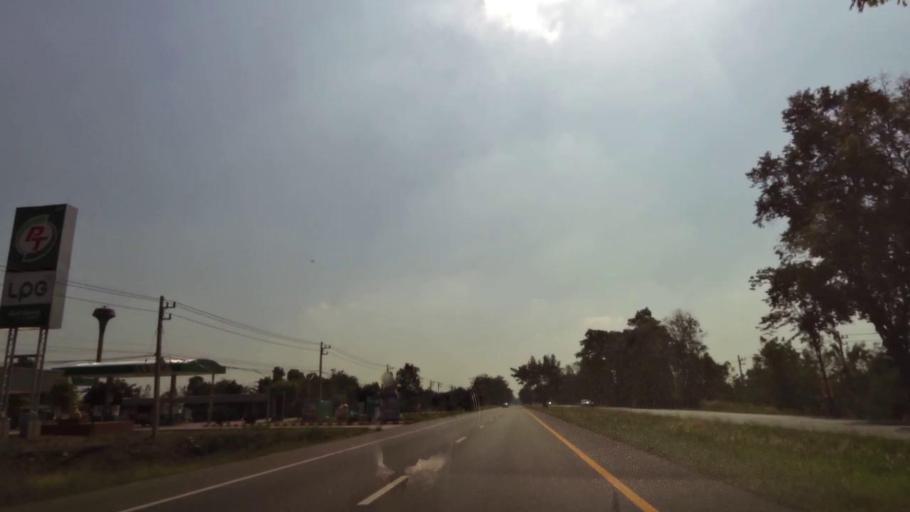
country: TH
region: Phichit
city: Bueng Na Rang
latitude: 16.2054
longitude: 100.1276
